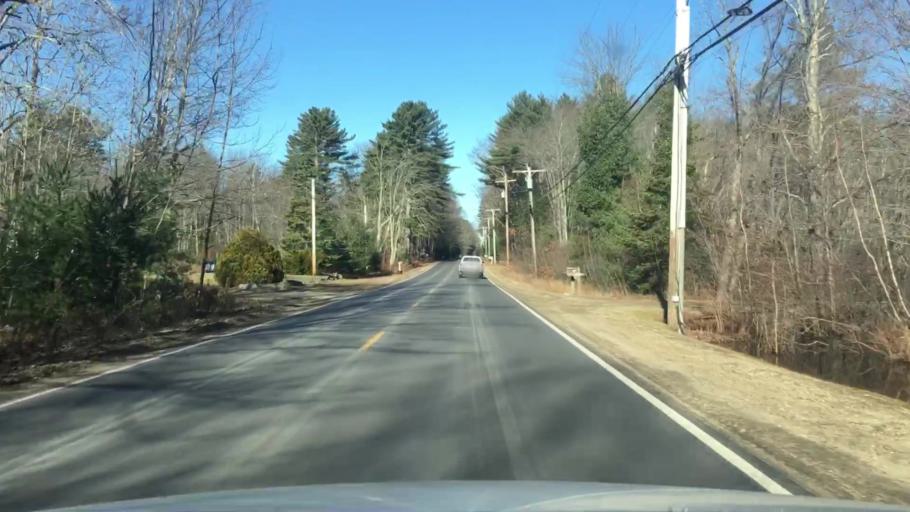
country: US
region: Maine
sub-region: York County
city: Arundel
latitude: 43.3887
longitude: -70.4808
